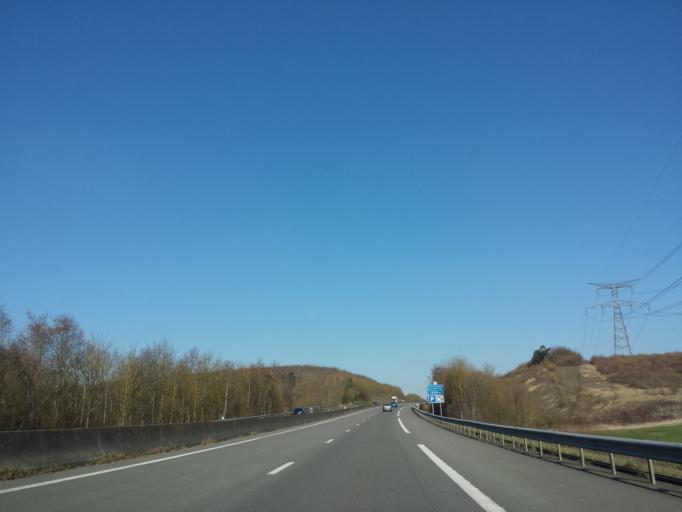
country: FR
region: Picardie
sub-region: Departement de la Somme
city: Conty
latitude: 49.7474
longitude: 2.2304
